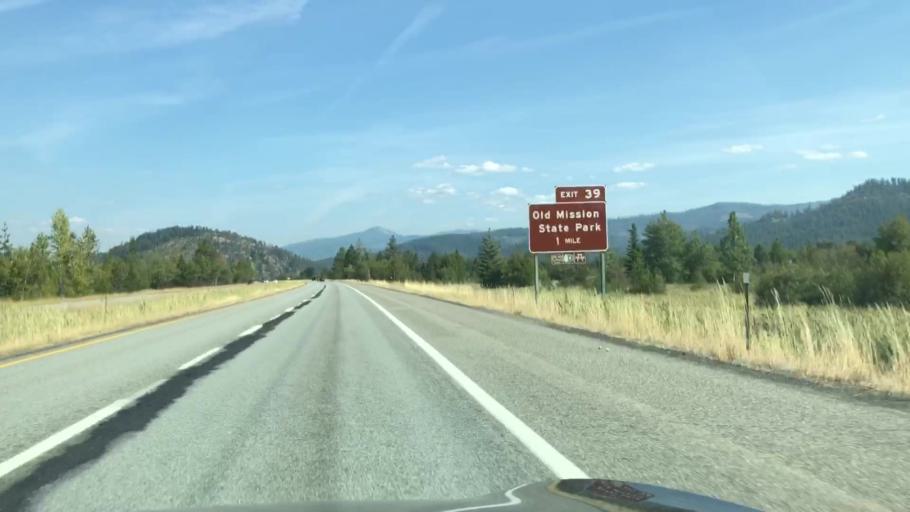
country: US
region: Idaho
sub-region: Shoshone County
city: Pinehurst
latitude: 47.5565
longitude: -116.3824
